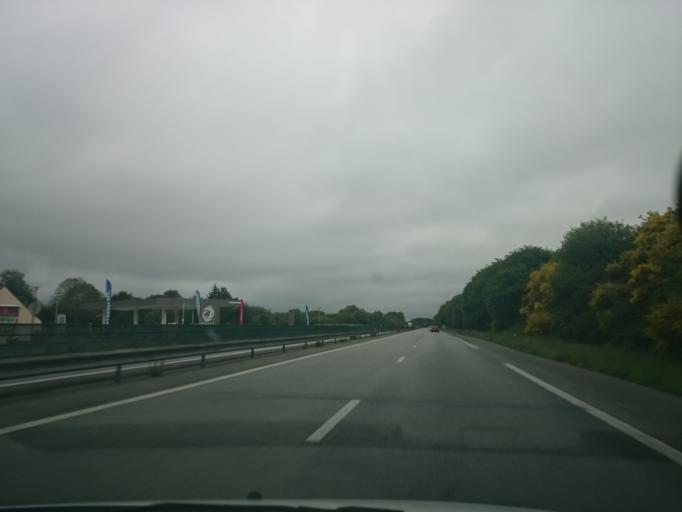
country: FR
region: Brittany
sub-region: Departement du Finistere
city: Saint-Yvi
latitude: 47.9593
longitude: -3.9566
